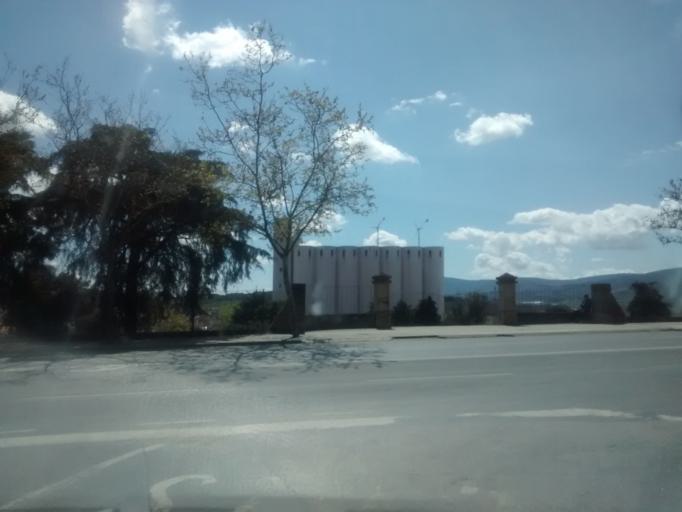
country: PT
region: Braganca
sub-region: Braganca Municipality
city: Braganca
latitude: 41.8021
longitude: -6.7694
